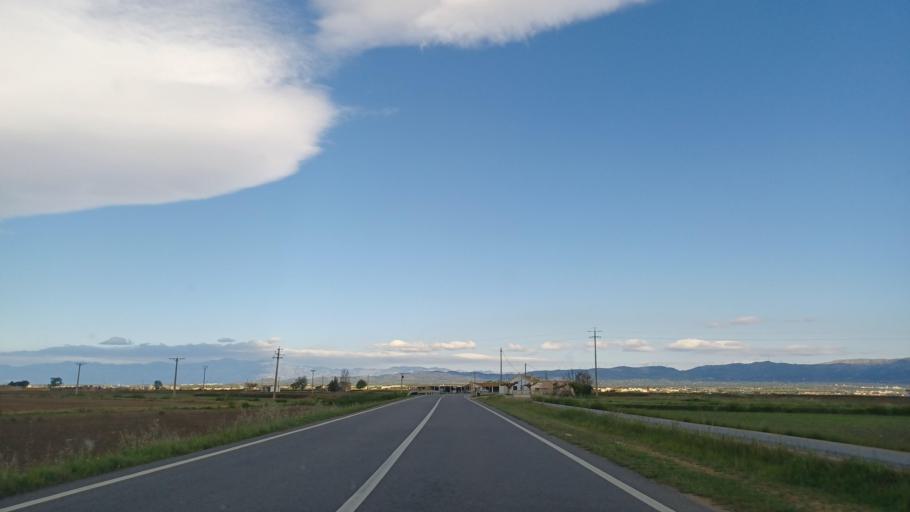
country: ES
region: Catalonia
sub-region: Provincia de Tarragona
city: Deltebre
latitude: 40.7503
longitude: 0.7077
